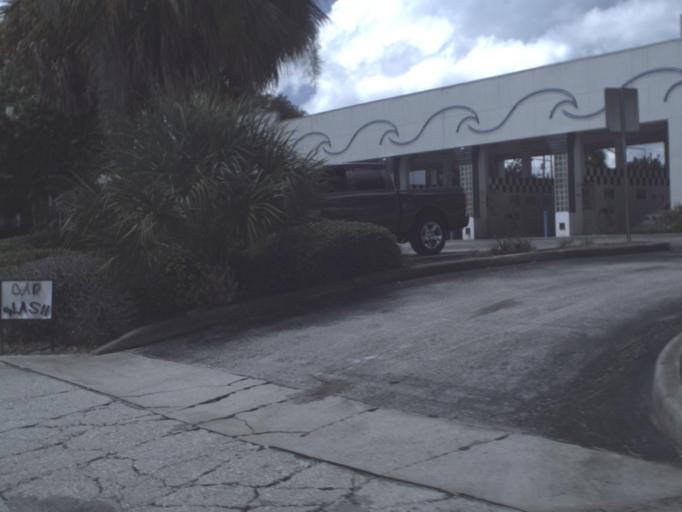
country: US
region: Florida
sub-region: Pinellas County
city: Seminole
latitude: 27.8584
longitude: -82.7872
